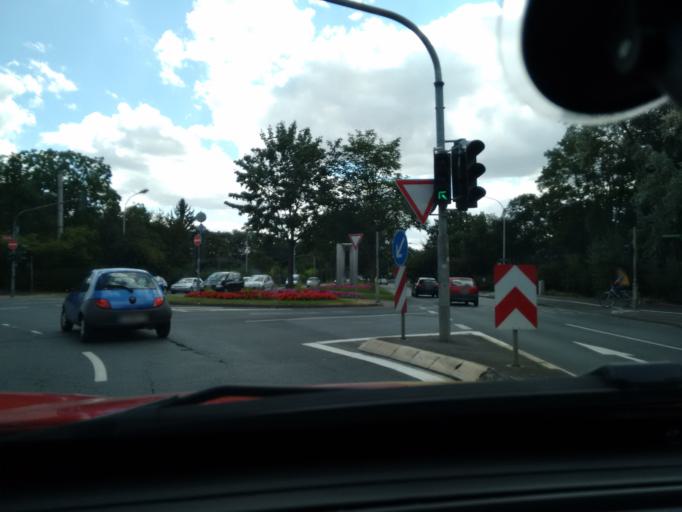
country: DE
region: Rheinland-Pfalz
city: Mainz
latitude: 49.9865
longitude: 8.2659
